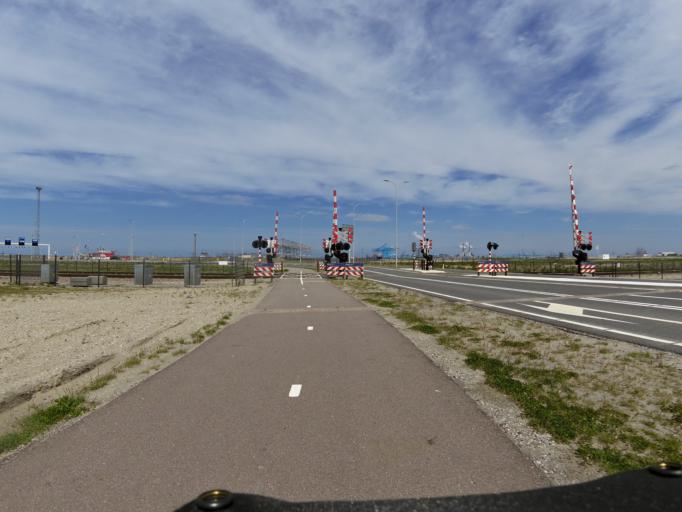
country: NL
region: South Holland
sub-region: Gemeente Goeree-Overflakkee
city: Goedereede
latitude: 51.9367
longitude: 3.9794
